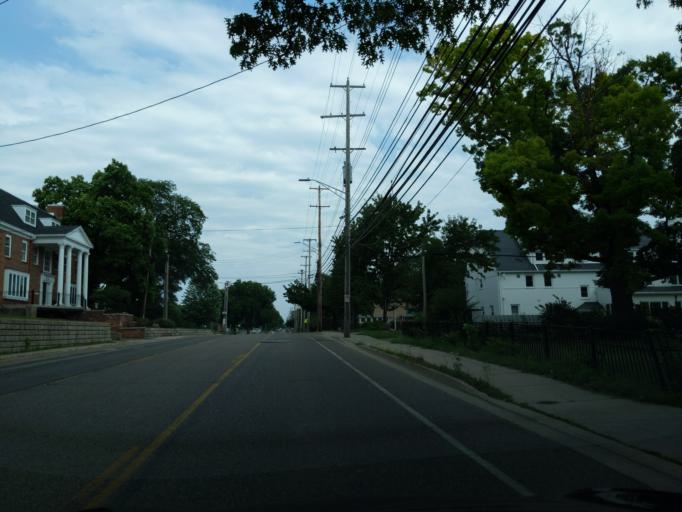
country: US
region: Michigan
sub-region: Ingham County
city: East Lansing
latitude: 42.7407
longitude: -84.4818
